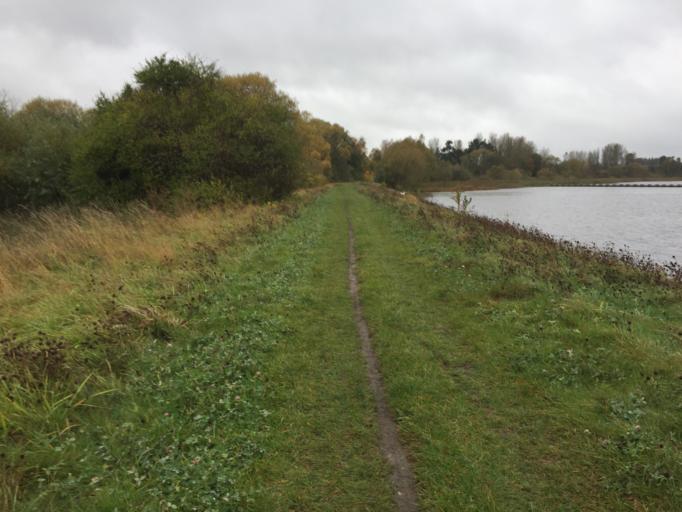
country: DK
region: Zealand
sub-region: Ringsted Kommune
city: Ringsted
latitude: 55.4818
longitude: 11.7528
